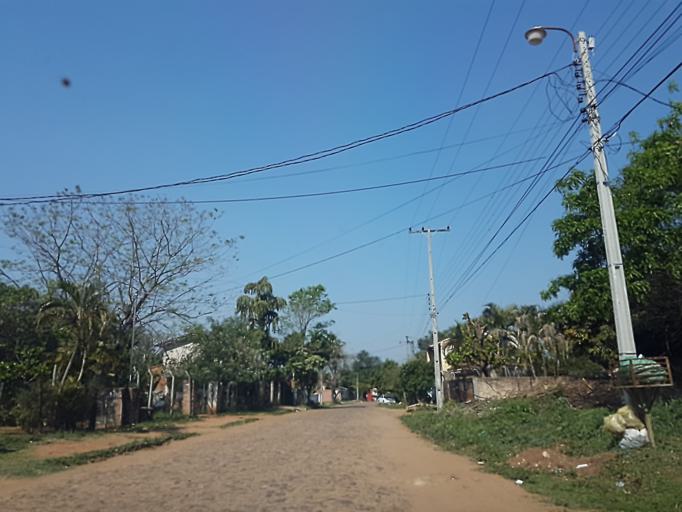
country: PY
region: Central
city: Colonia Mariano Roque Alonso
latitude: -25.2136
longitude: -57.5215
